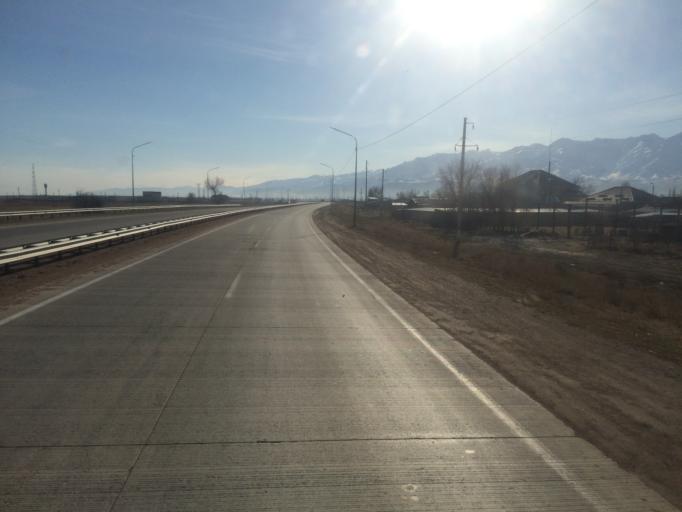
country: KG
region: Talas
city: Ivanovo-Alekseyevka
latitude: 42.9945
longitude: 72.1088
